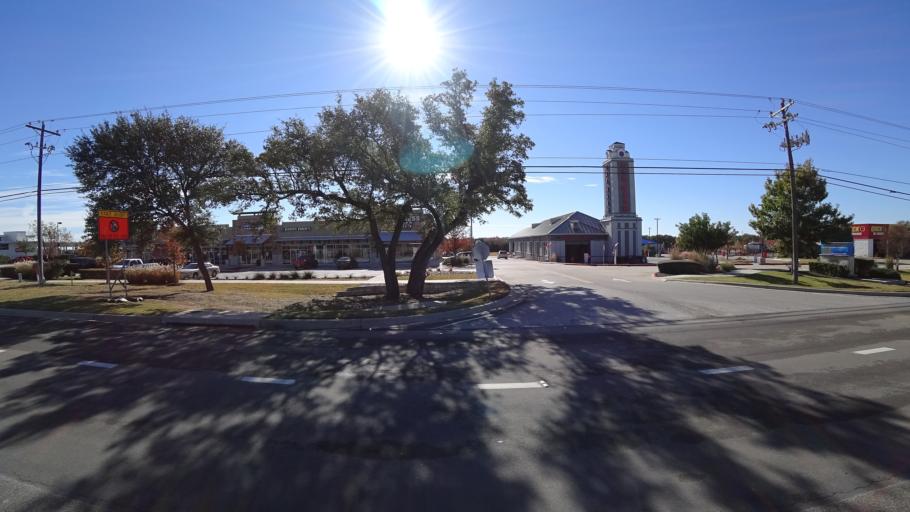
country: US
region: Texas
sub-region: Williamson County
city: Cedar Park
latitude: 30.5262
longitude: -97.8127
